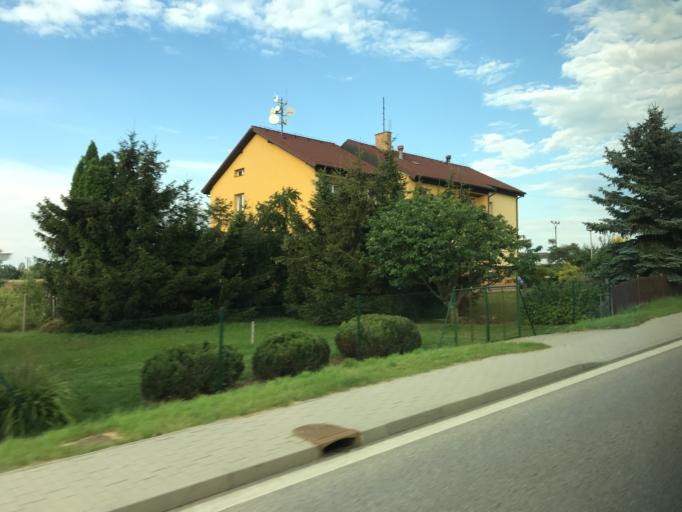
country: CZ
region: Jihocesky
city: Lisov
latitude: 49.0007
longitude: 14.6568
